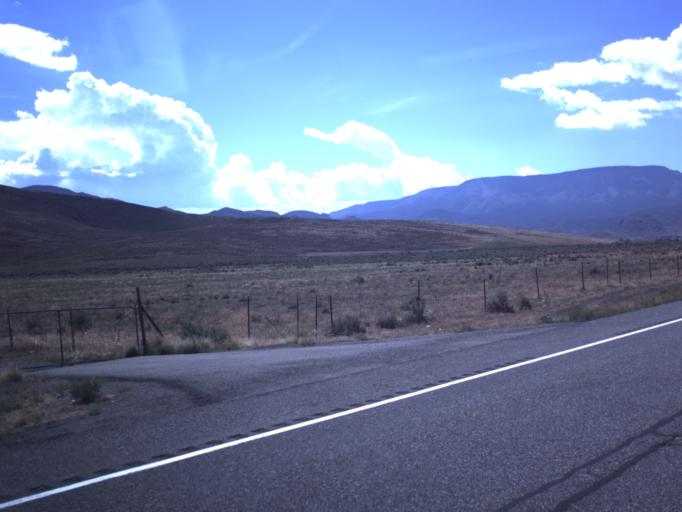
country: US
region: Utah
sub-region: Piute County
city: Junction
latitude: 38.2633
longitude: -112.2213
